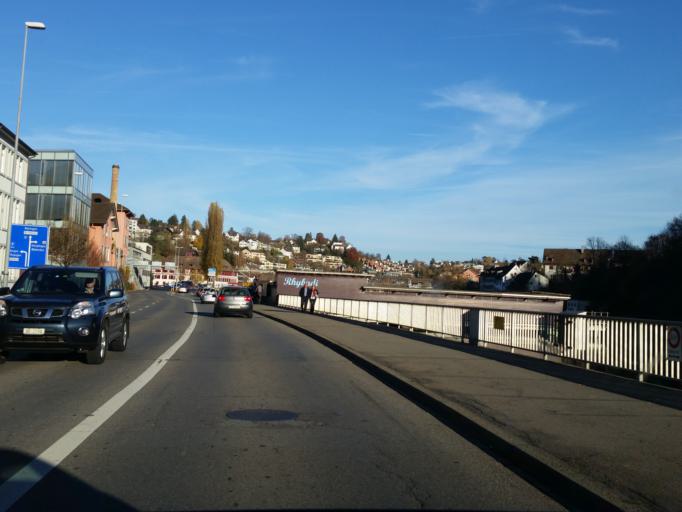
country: CH
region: Schaffhausen
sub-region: Bezirk Schaffhausen
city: Schaffhausen
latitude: 47.6937
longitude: 8.6364
